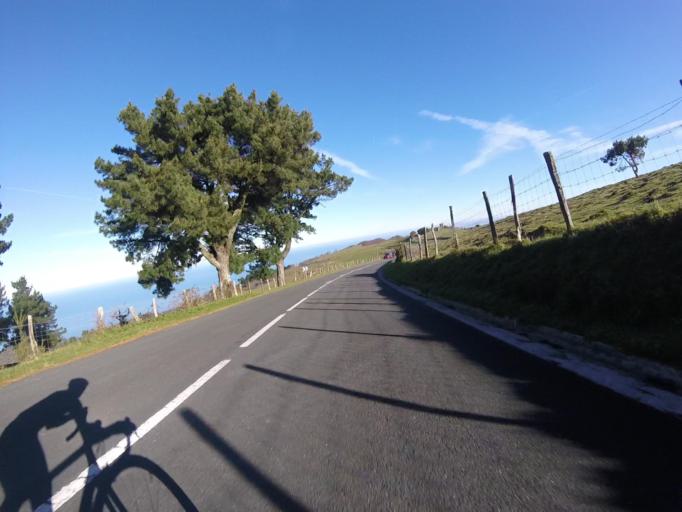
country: ES
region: Basque Country
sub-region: Provincia de Guipuzcoa
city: Fuenterrabia
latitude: 43.3515
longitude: -1.8452
